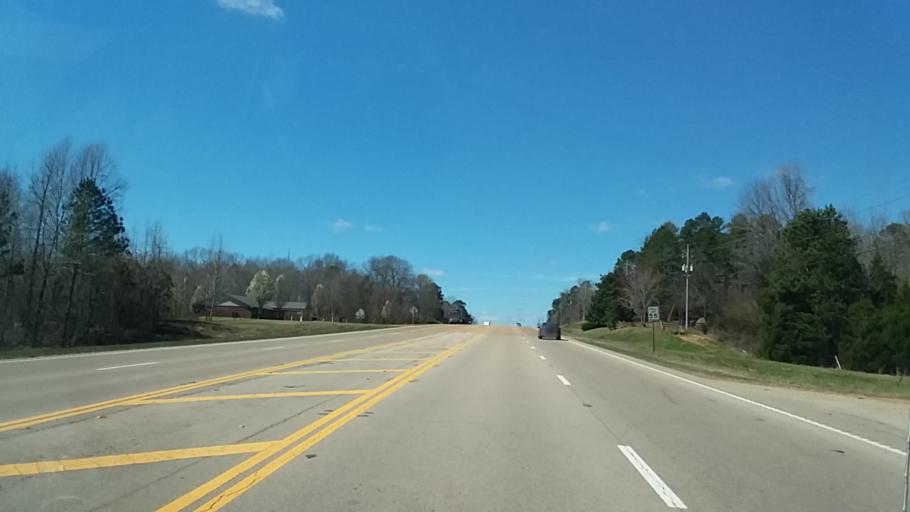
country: US
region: Mississippi
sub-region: Alcorn County
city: Farmington
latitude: 34.8937
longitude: -88.4666
